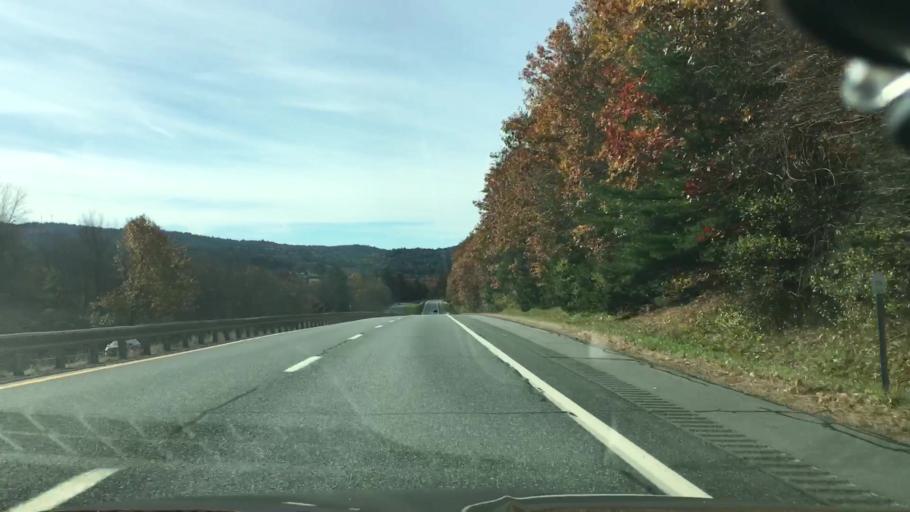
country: US
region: New Hampshire
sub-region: Cheshire County
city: Westmoreland
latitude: 42.9768
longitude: -72.4842
